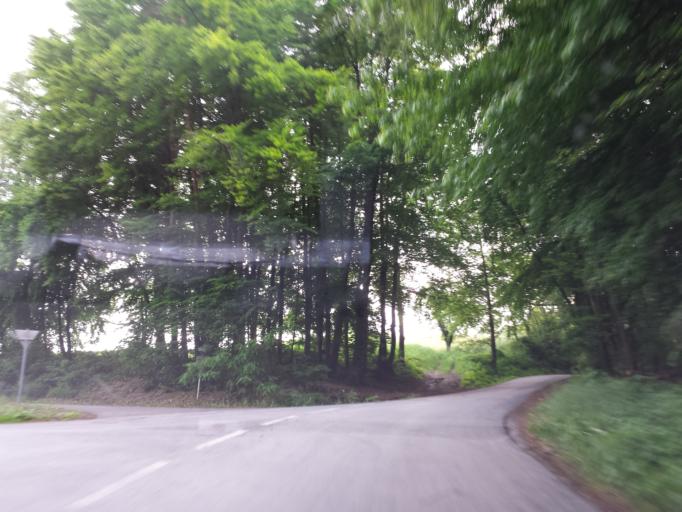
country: AT
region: Styria
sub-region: Politischer Bezirk Weiz
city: Sankt Ruprecht an der Raab
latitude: 47.1211
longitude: 15.6521
